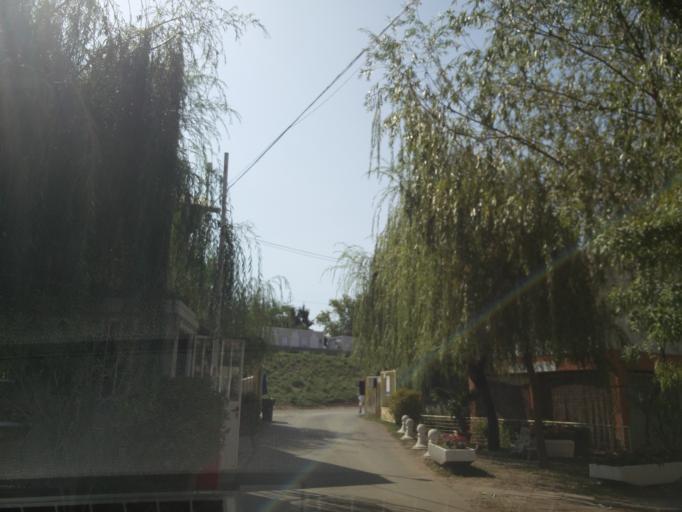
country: HU
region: Csongrad
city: Szeged
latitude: 46.2527
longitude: 20.1596
